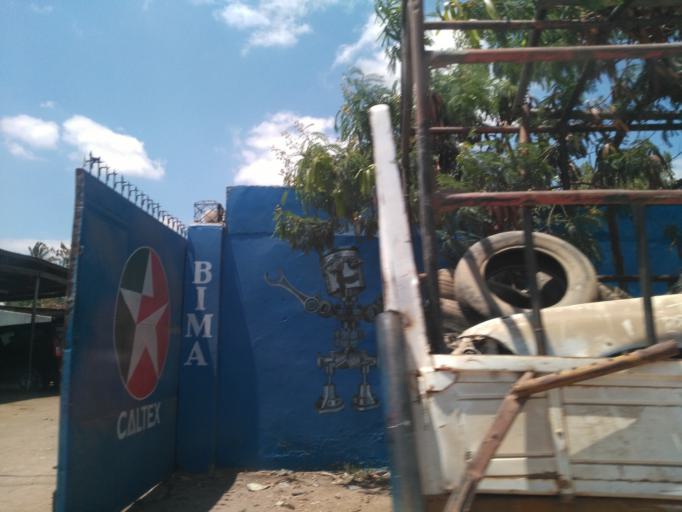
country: TZ
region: Dodoma
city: Dodoma
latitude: -6.1750
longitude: 35.7542
